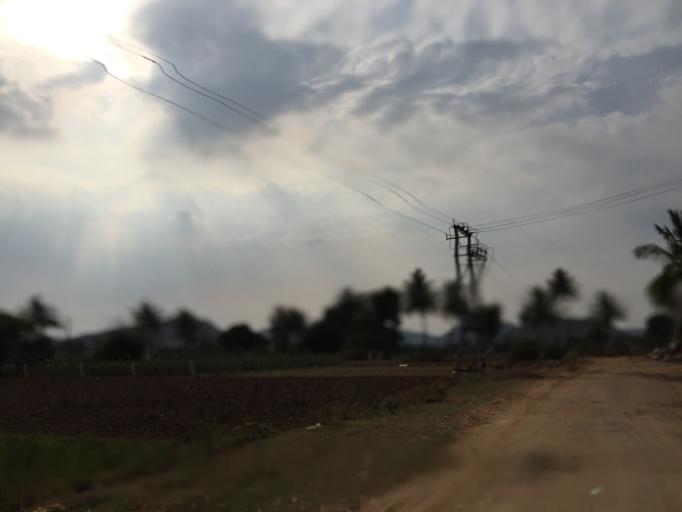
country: IN
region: Karnataka
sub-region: Chikkaballapur
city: Gudibanda
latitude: 13.5740
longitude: 77.7269
